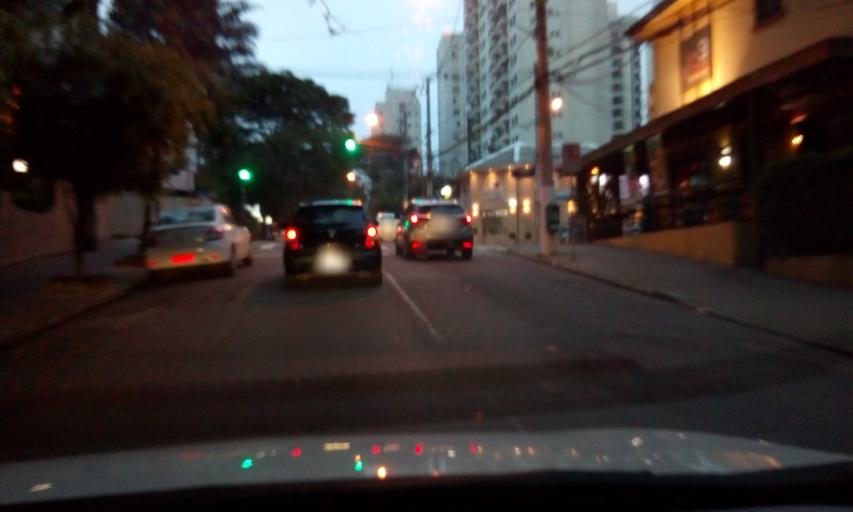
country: BR
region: Sao Paulo
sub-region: Sao Paulo
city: Sao Paulo
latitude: -23.6044
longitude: -46.6663
